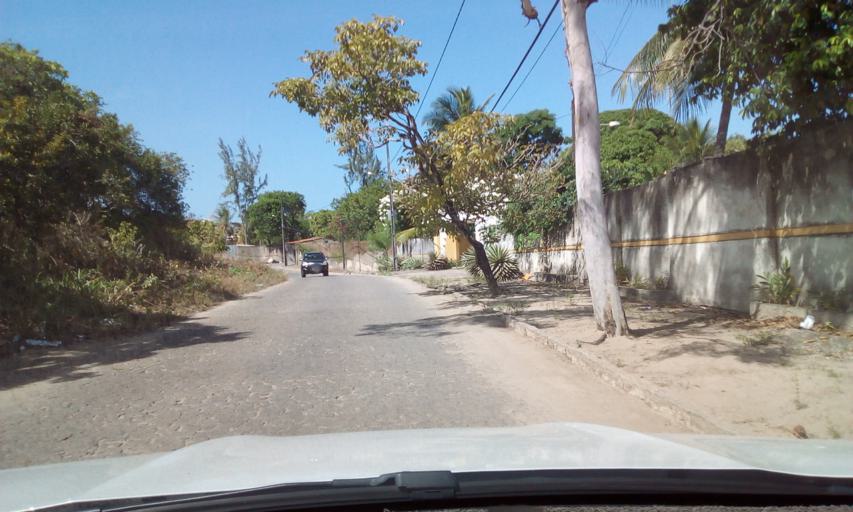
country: BR
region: Paraiba
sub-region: Joao Pessoa
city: Joao Pessoa
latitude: -7.1569
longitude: -34.8455
